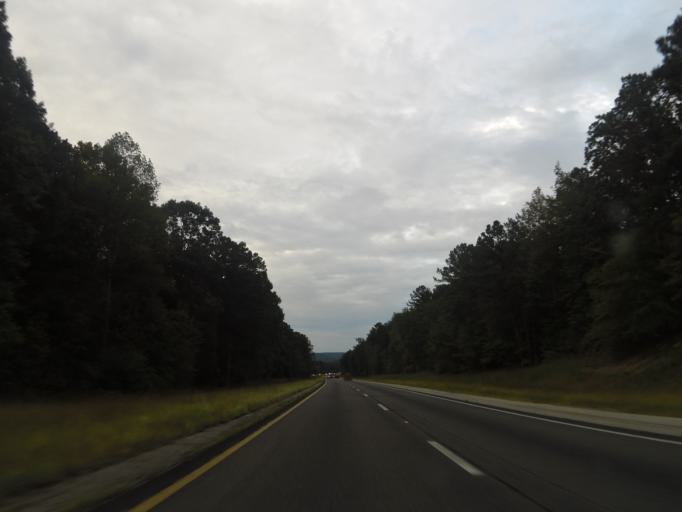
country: US
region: Alabama
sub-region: Saint Clair County
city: Springville
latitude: 33.7372
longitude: -86.4902
